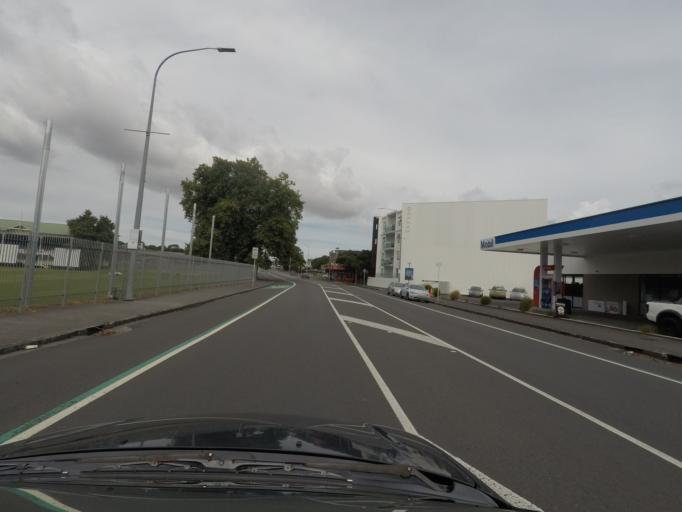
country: NZ
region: Auckland
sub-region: Auckland
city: Auckland
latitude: -36.8740
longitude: 174.7422
